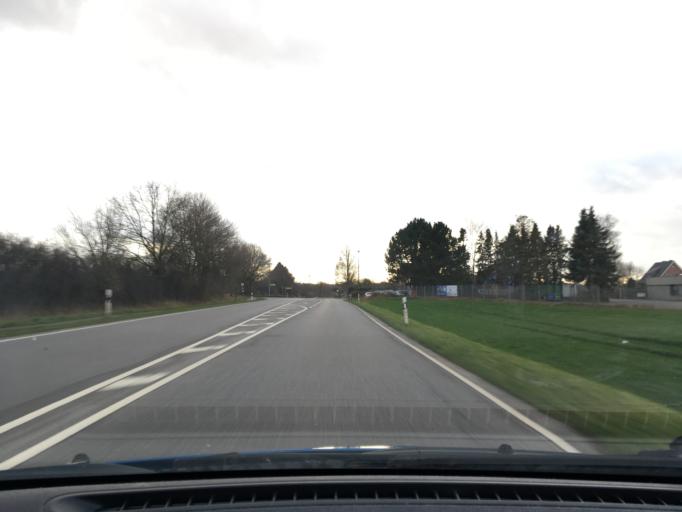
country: DE
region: Schleswig-Holstein
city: Ottenbuttel
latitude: 53.9736
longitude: 9.4963
